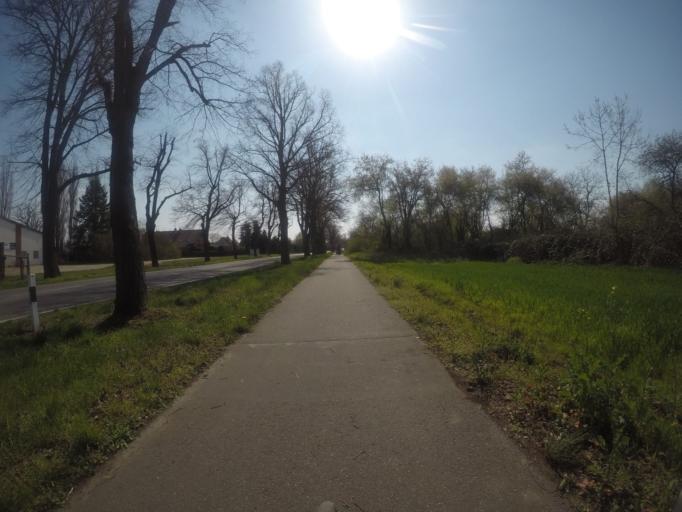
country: DE
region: Brandenburg
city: Nauen
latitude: 52.5828
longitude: 12.8750
